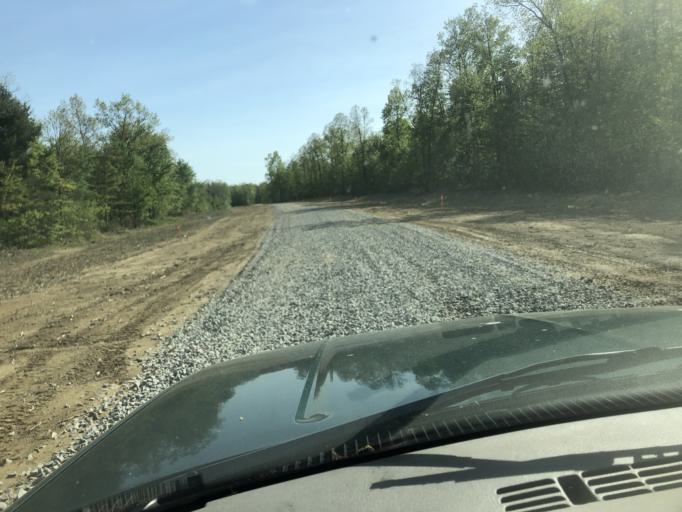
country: US
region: Tennessee
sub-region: Fentress County
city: Jamestown
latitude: 36.3191
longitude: -84.8530
